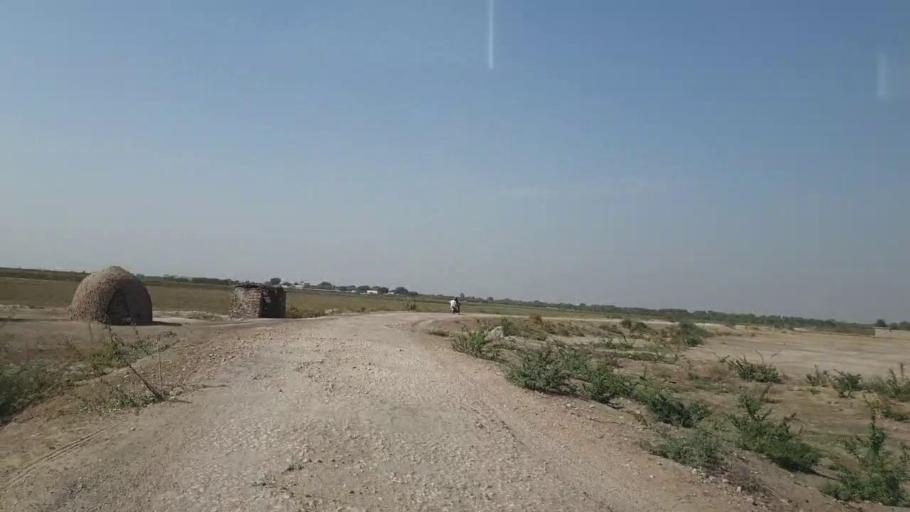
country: PK
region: Sindh
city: Nabisar
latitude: 25.0181
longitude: 69.5248
